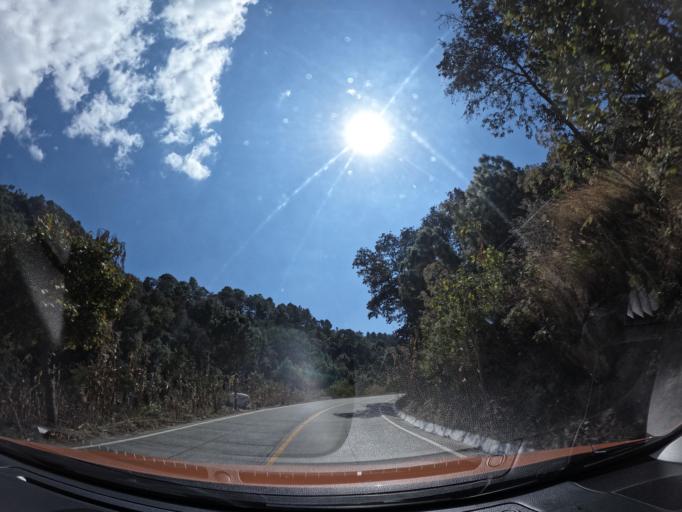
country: GT
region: Solola
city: San Antonio Palopo
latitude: 14.6948
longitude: -91.0709
